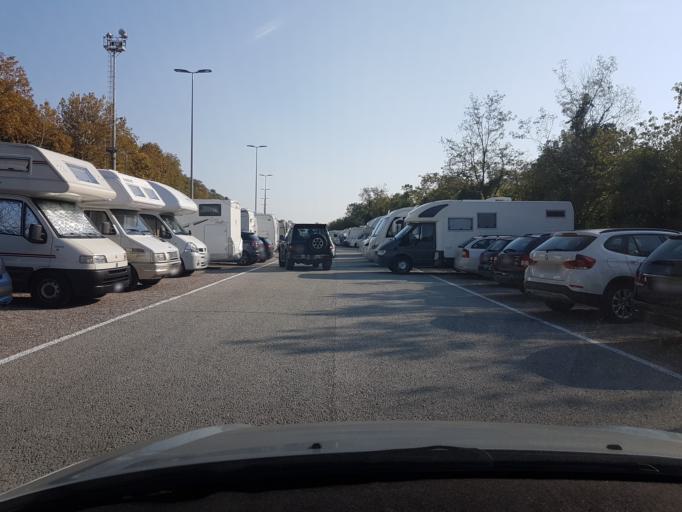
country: IT
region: Friuli Venezia Giulia
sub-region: Provincia di Trieste
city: Villa Opicina
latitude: 45.6763
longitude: 13.7544
